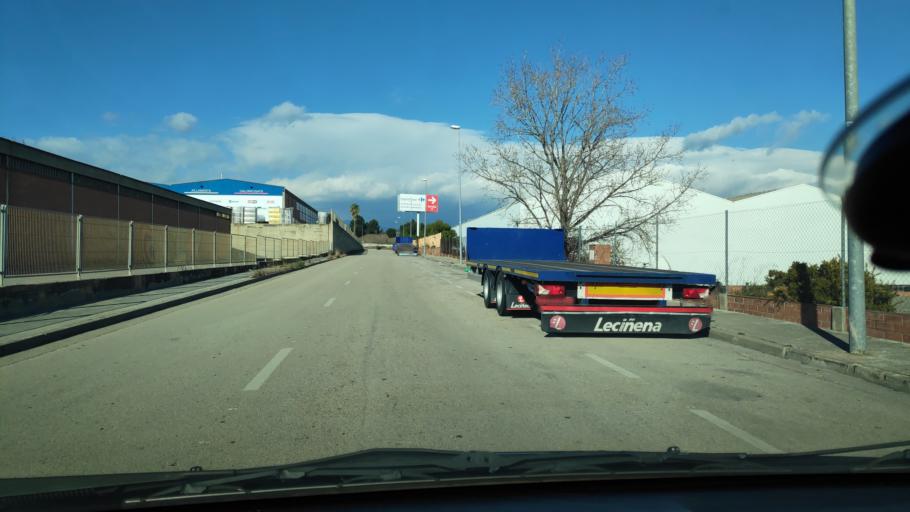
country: ES
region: Catalonia
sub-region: Provincia de Barcelona
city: Sant Quirze del Valles
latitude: 41.5406
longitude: 2.0782
